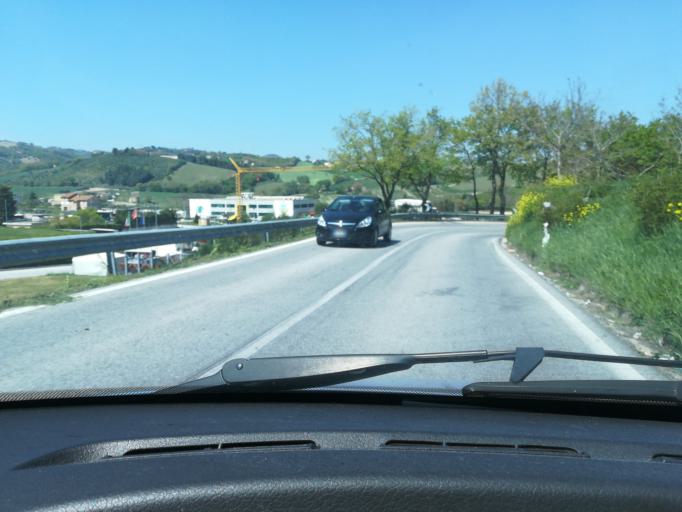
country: IT
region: The Marches
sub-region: Provincia di Macerata
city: Strada
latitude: 43.4039
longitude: 13.2050
